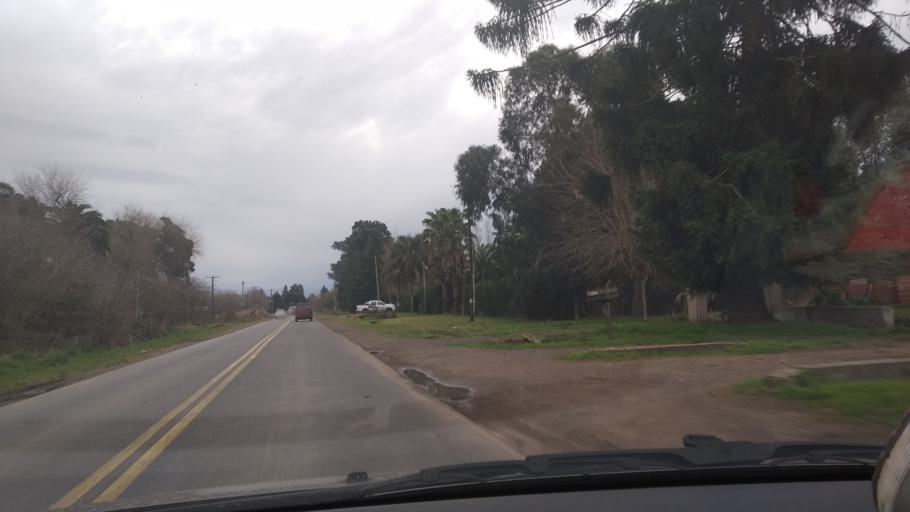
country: AR
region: Buenos Aires
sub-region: Partido de La Plata
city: La Plata
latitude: -34.9979
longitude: -58.0705
